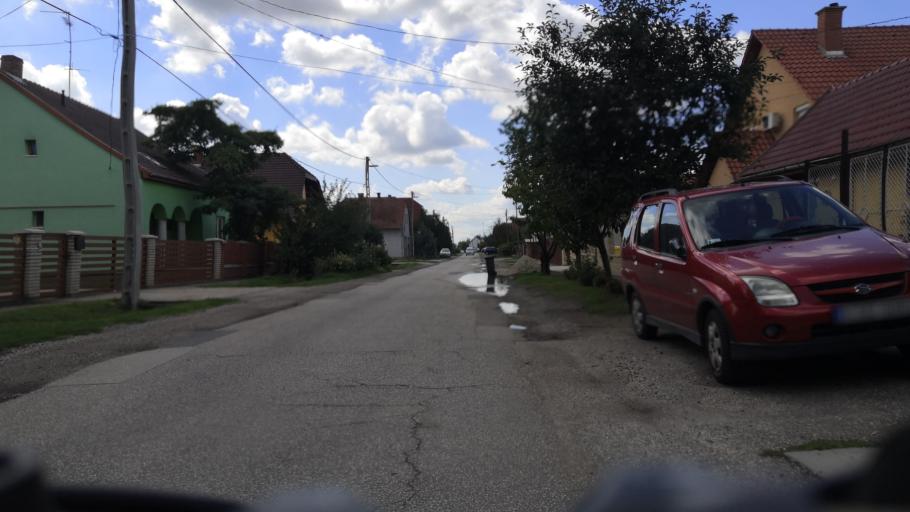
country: HU
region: Csongrad
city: Szeged
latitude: 46.2780
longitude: 20.1125
